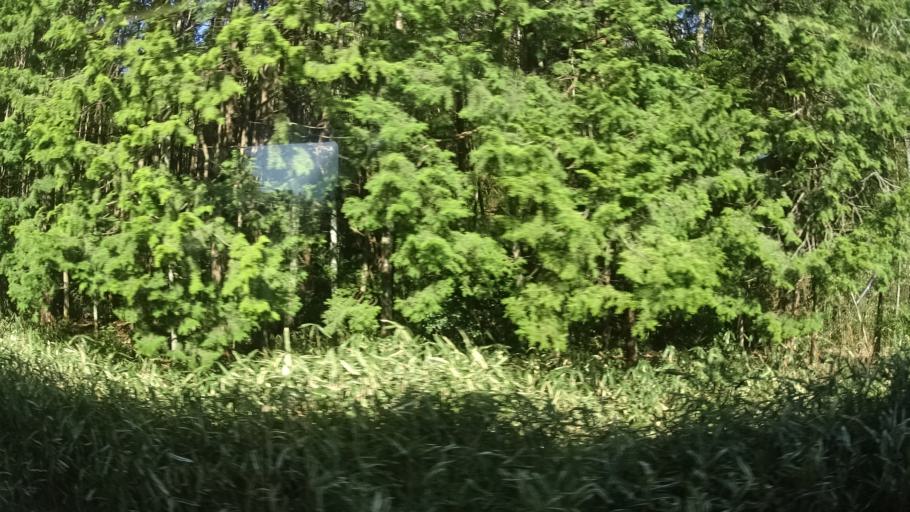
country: JP
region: Fukushima
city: Namie
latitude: 37.5359
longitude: 140.9866
